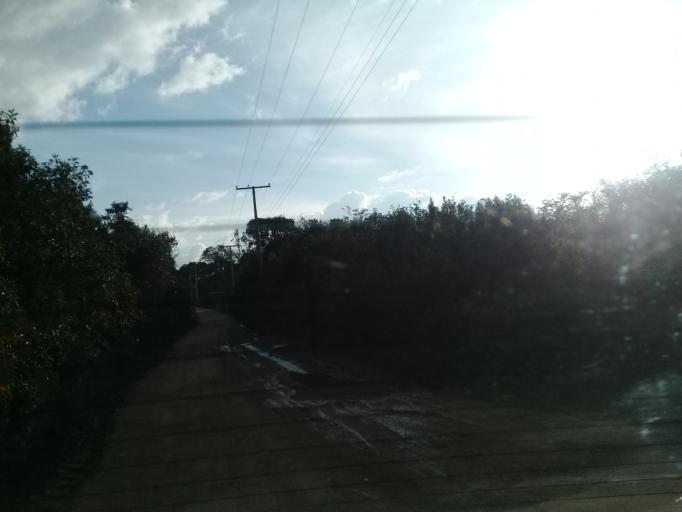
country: CO
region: Cundinamarca
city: Sibate
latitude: 4.4437
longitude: -74.2789
